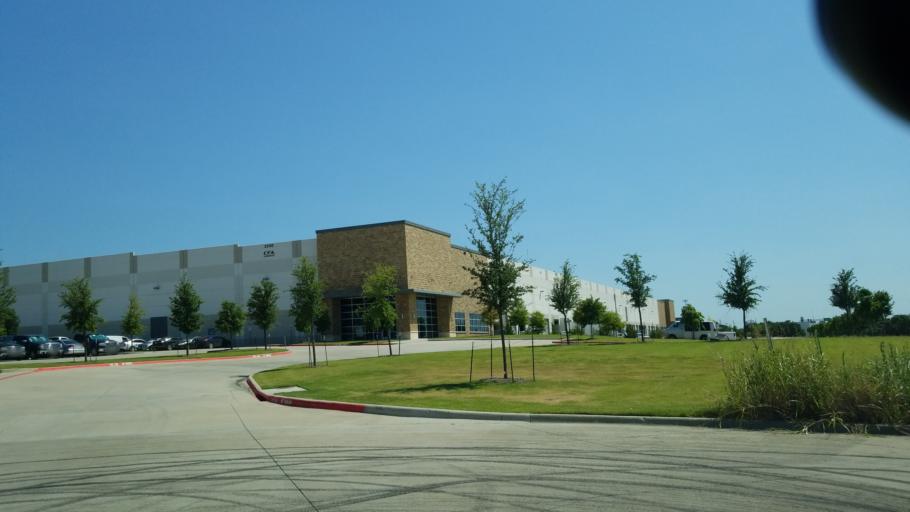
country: US
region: Texas
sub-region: Dallas County
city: Farmers Branch
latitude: 32.9134
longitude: -96.9057
